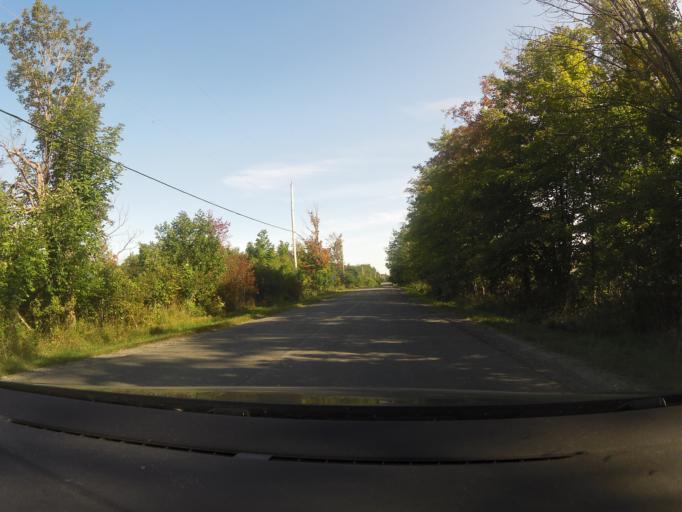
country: CA
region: Ontario
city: Carleton Place
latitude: 45.2731
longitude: -76.0619
